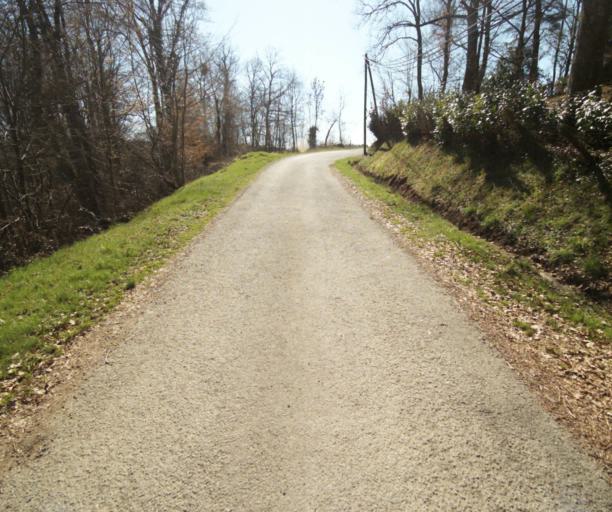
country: FR
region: Limousin
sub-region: Departement de la Correze
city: Saint-Mexant
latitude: 45.3005
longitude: 1.6204
